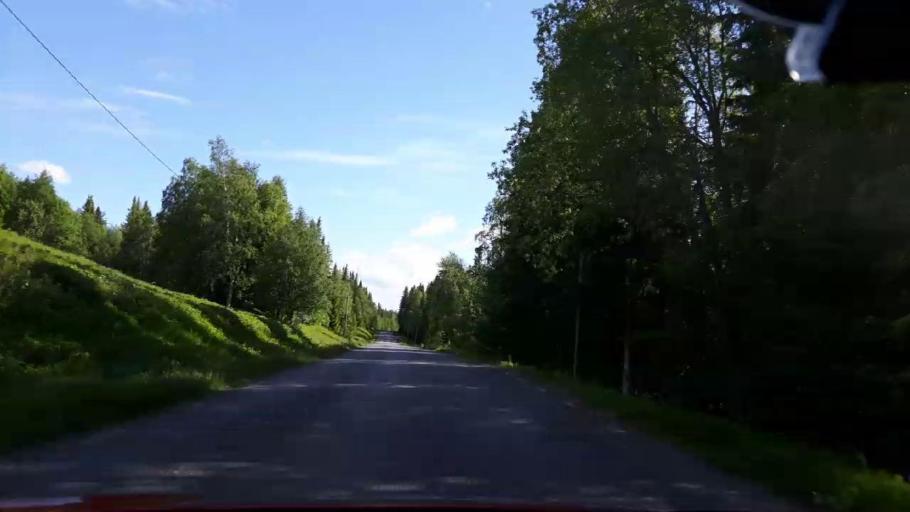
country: SE
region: Jaemtland
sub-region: Krokoms Kommun
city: Valla
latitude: 63.7488
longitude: 14.1174
